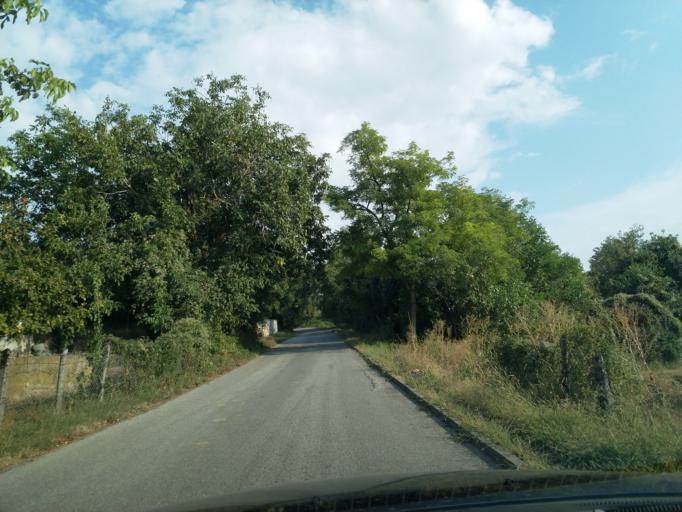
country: RS
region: Central Serbia
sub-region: Pomoravski Okrug
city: Paracin
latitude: 43.8500
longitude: 21.5309
